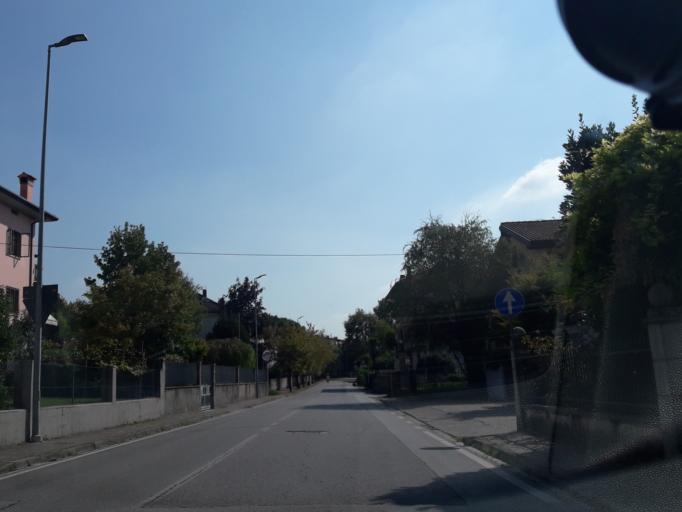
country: IT
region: Friuli Venezia Giulia
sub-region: Provincia di Udine
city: Tavagnacco
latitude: 46.1151
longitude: 13.2106
